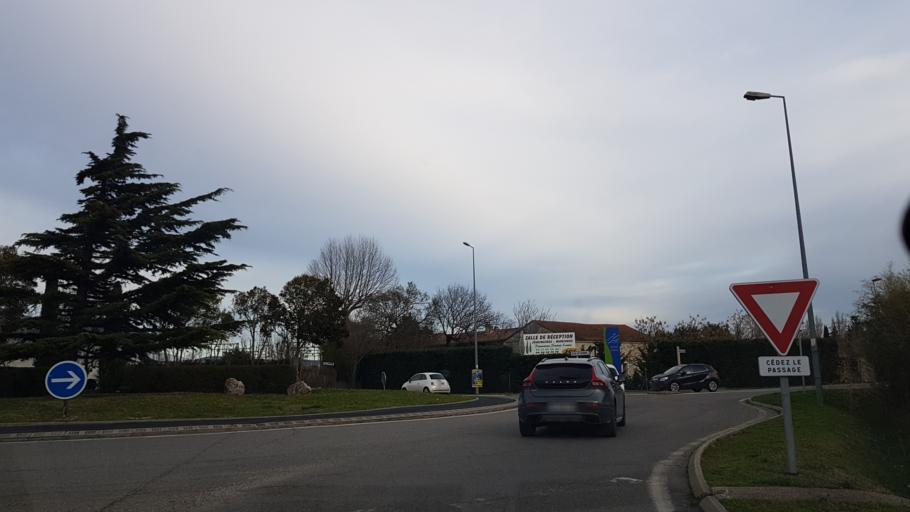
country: FR
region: Provence-Alpes-Cote d'Azur
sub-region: Departement du Vaucluse
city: Le Thor
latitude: 43.9222
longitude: 5.0185
